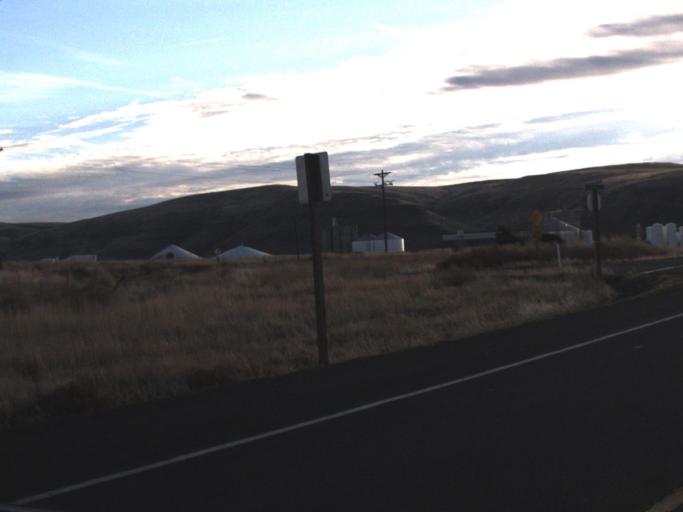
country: US
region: Washington
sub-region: Garfield County
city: Pomeroy
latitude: 46.6341
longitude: -117.8083
